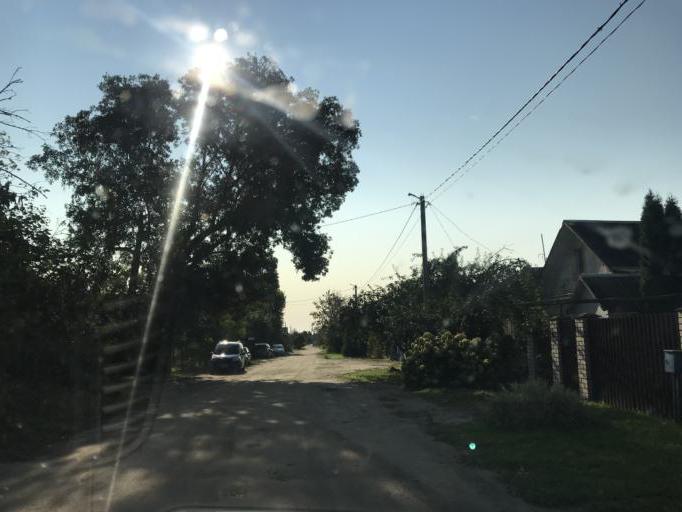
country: BY
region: Mogilev
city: Buynichy
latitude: 53.8808
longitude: 30.2688
